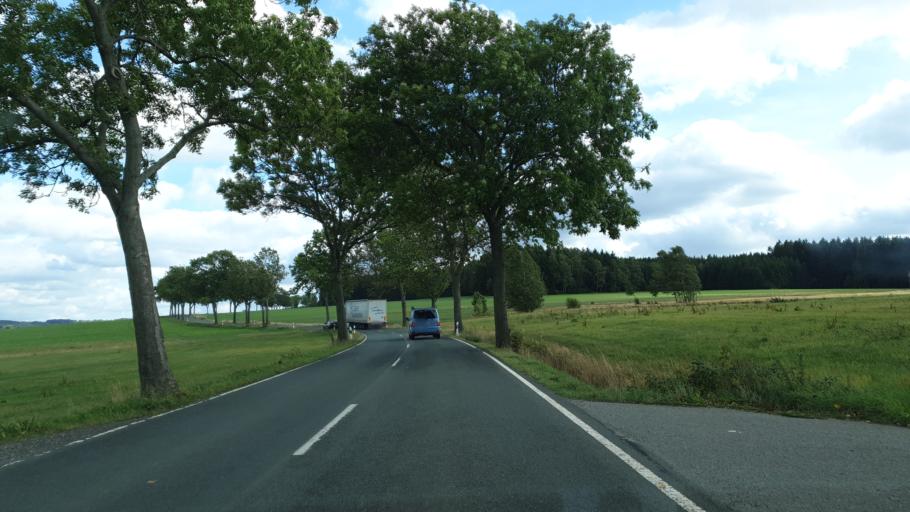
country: DE
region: Saxony
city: Lossnitz
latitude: 50.6538
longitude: 12.7120
